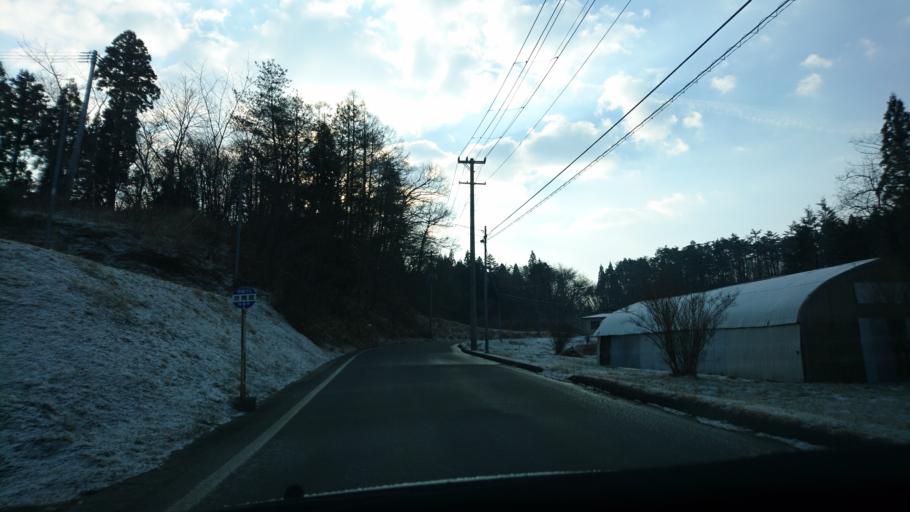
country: JP
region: Iwate
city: Ichinoseki
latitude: 38.9117
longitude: 141.3687
